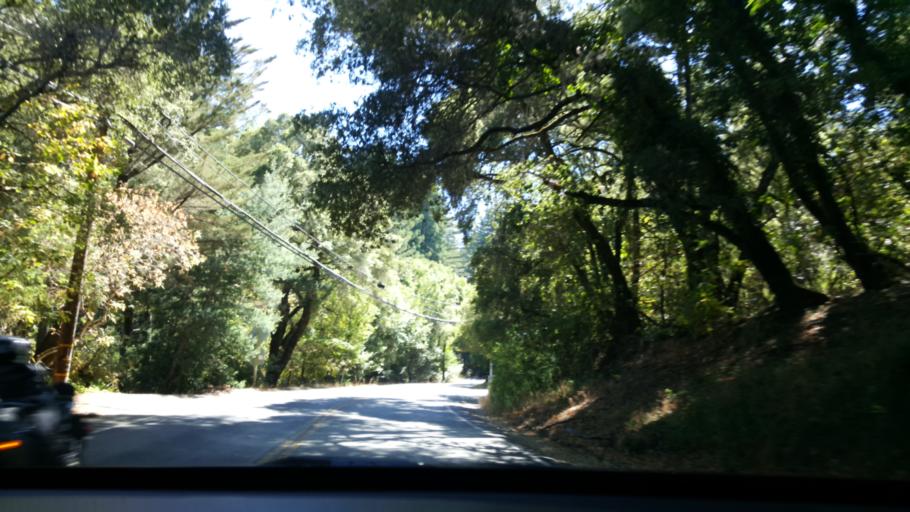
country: US
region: California
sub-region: San Mateo County
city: Portola Valley
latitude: 37.3930
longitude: -122.2609
